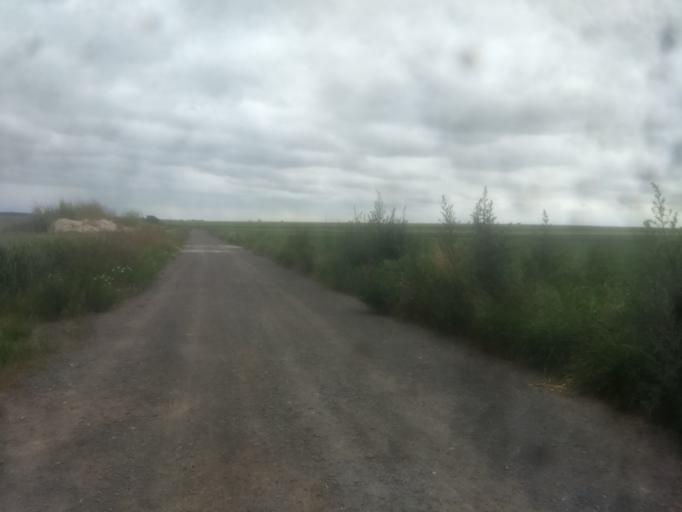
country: FR
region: Nord-Pas-de-Calais
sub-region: Departement du Pas-de-Calais
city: Neuville-Saint-Vaast
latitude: 50.3509
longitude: 2.7384
